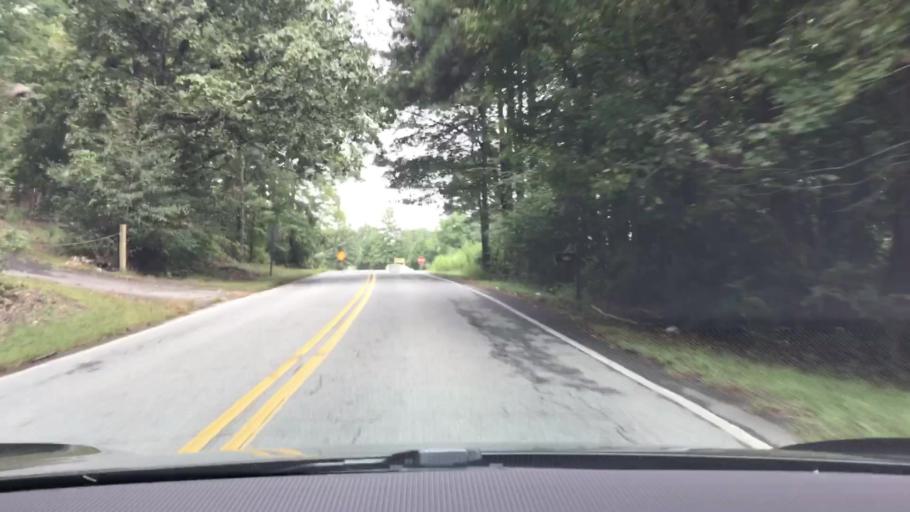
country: US
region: Georgia
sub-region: Barrow County
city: Auburn
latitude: 34.0719
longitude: -83.8426
